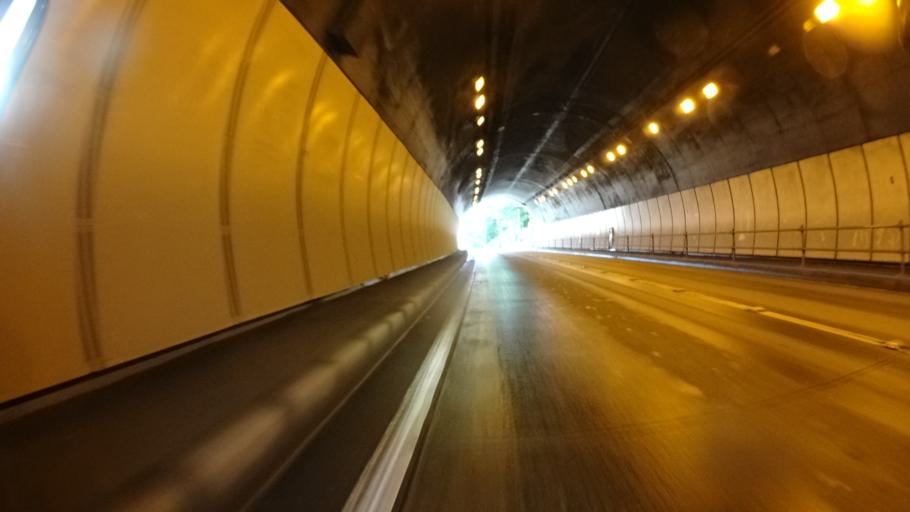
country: JP
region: Tokyo
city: Ome
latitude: 35.8166
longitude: 139.2477
